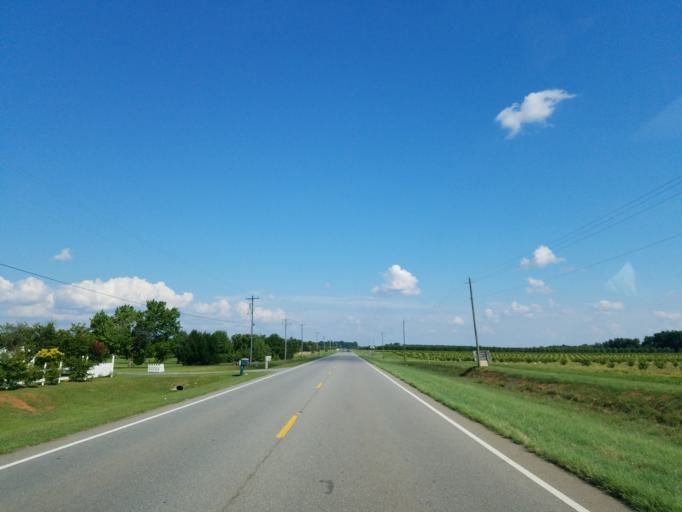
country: US
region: Georgia
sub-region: Peach County
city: Fort Valley
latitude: 32.6109
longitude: -83.9527
